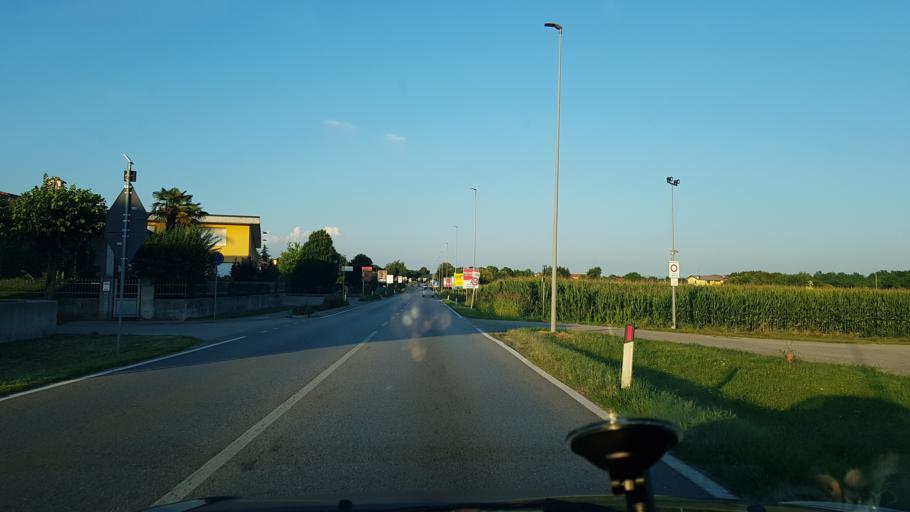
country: IT
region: Friuli Venezia Giulia
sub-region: Provincia di Udine
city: Fagagna
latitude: 46.0983
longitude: 13.0989
